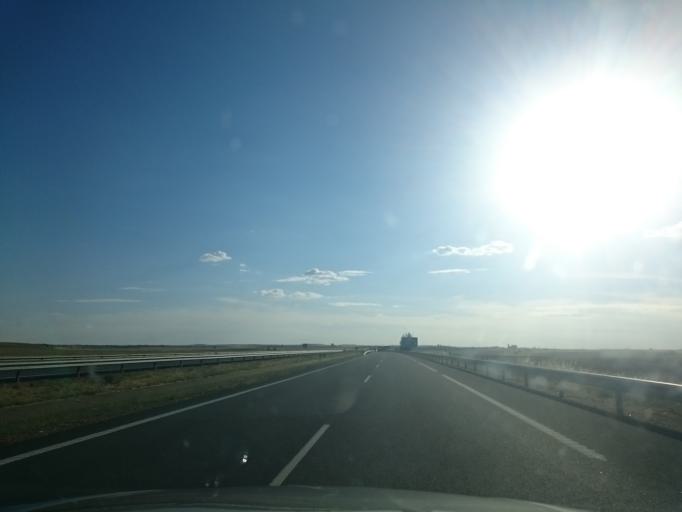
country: ES
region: Castille and Leon
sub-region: Provincia de Burgos
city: Padilla de Abajo
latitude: 42.4036
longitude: -4.1937
